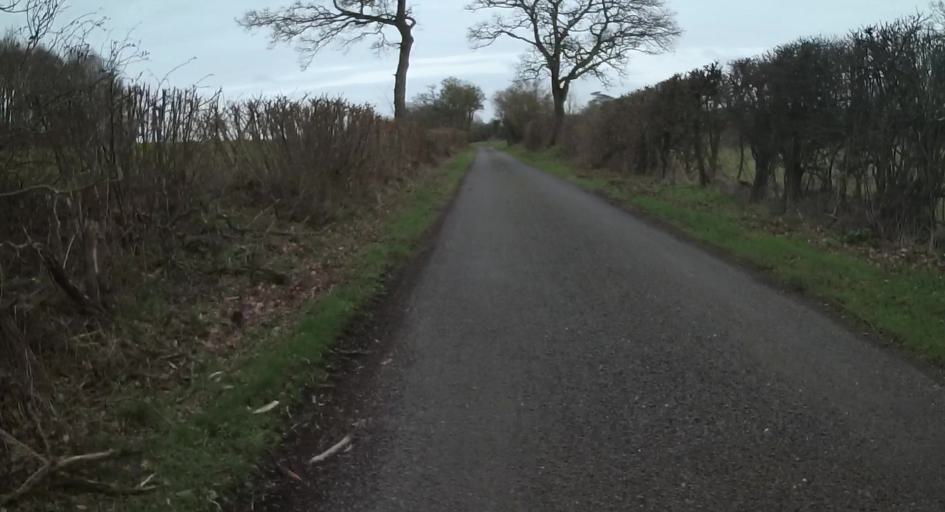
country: GB
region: England
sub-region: Hampshire
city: Overton
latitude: 51.2649
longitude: -1.2459
